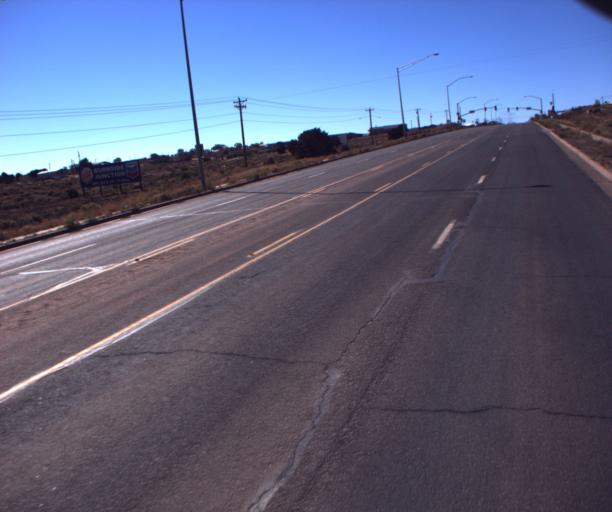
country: US
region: Arizona
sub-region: Apache County
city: Saint Michaels
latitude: 35.6579
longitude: -109.0865
